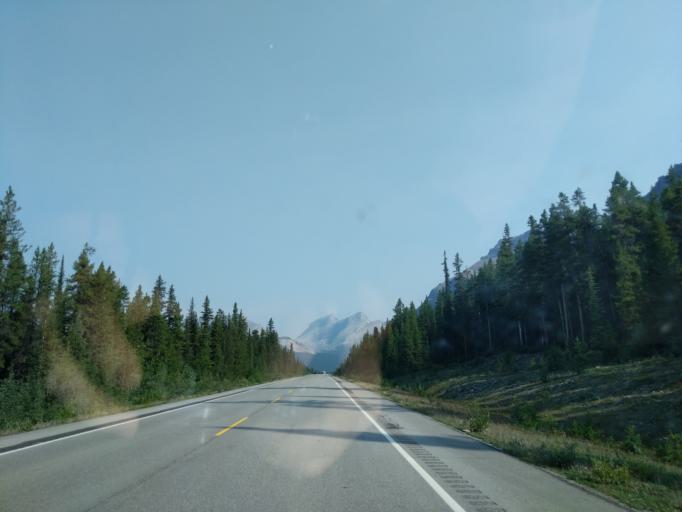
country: CA
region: Alberta
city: Lake Louise
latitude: 51.6069
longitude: -116.3119
